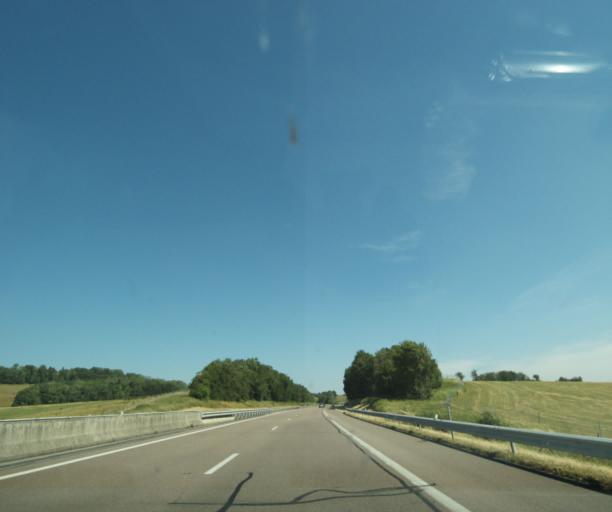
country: FR
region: Lorraine
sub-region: Departement des Vosges
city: Chatenois
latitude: 48.3875
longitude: 5.8805
